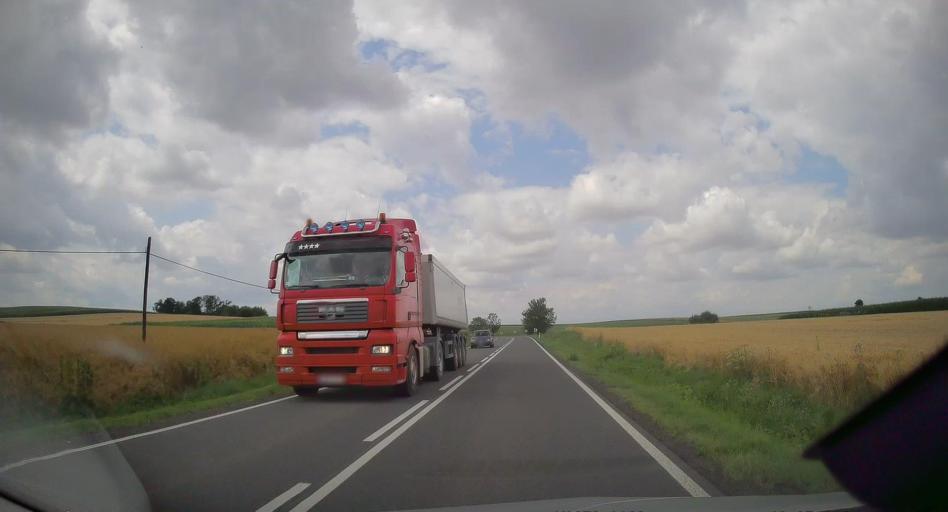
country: PL
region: Opole Voivodeship
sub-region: Powiat prudnicki
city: Glogowek
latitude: 50.3543
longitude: 17.8294
